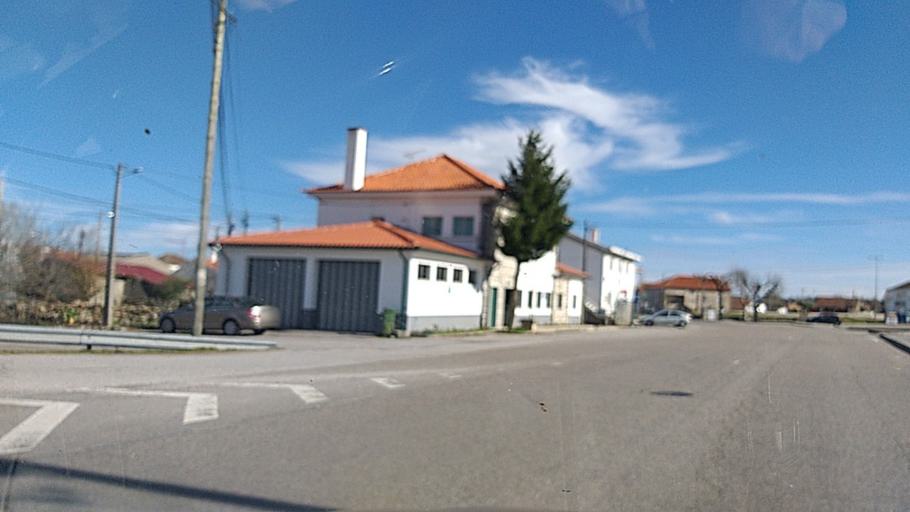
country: PT
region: Guarda
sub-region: Guarda
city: Sequeira
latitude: 40.6019
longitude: -7.0695
